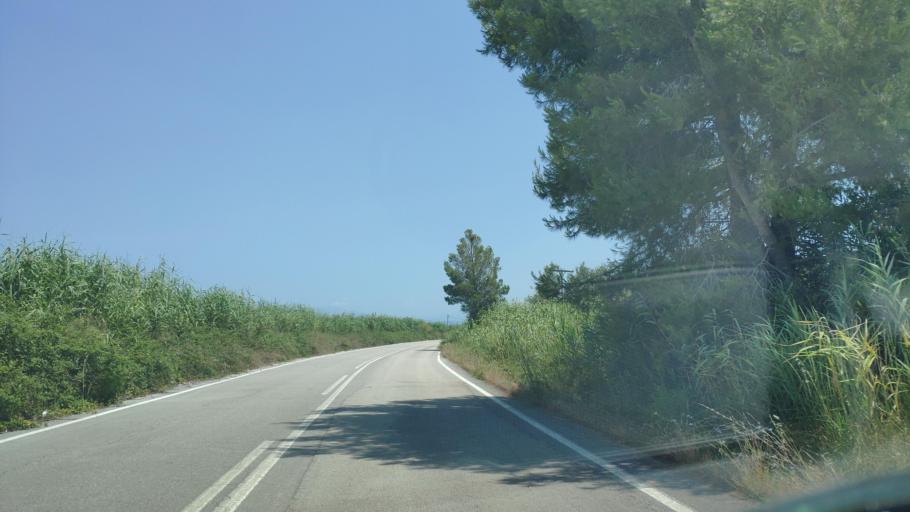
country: GR
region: Epirus
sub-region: Nomos Artas
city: Aneza
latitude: 39.0592
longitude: 20.8676
